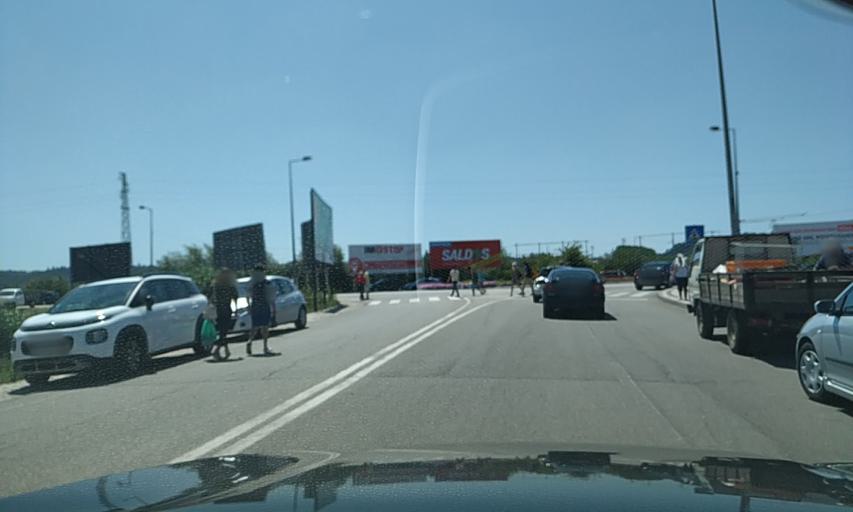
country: PT
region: Aveiro
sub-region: Agueda
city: Agueda
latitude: 40.5719
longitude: -8.4410
